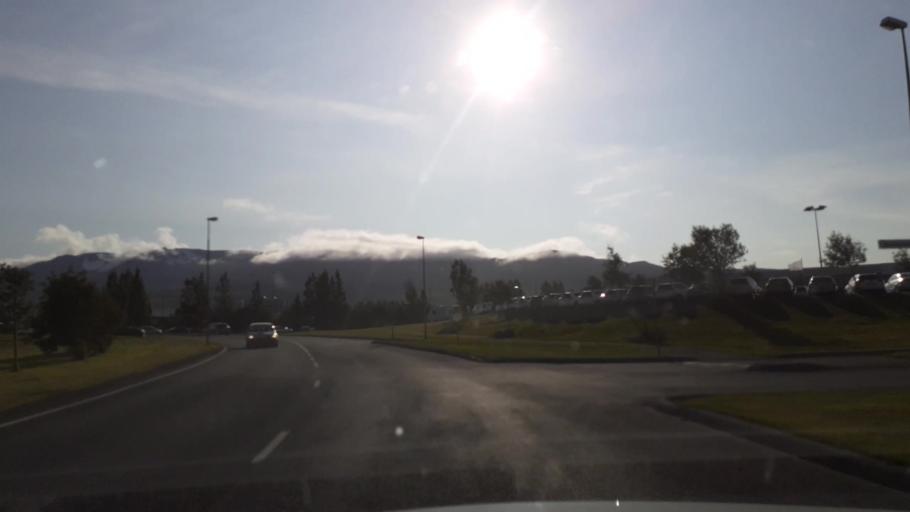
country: IS
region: Northeast
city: Akureyri
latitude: 65.6966
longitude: -18.1215
